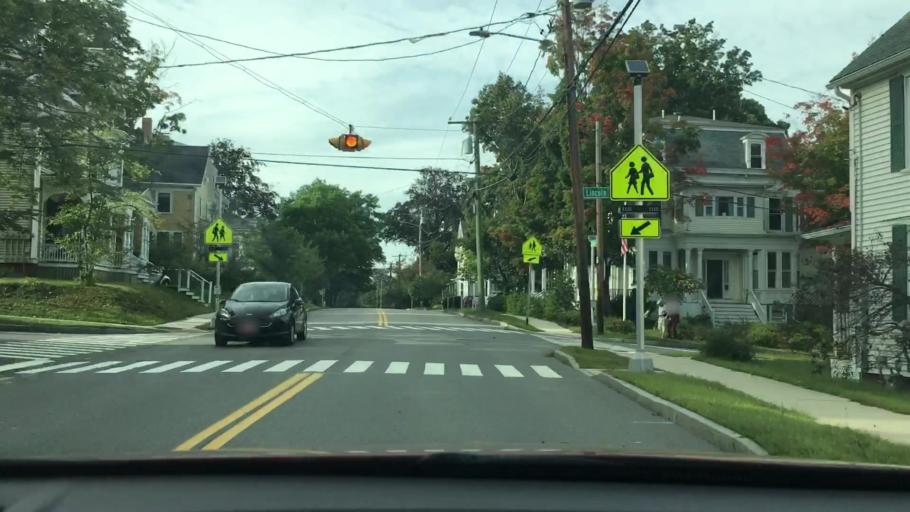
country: US
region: New Hampshire
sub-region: Rockingham County
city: Portsmouth
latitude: 43.0683
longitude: -70.7594
